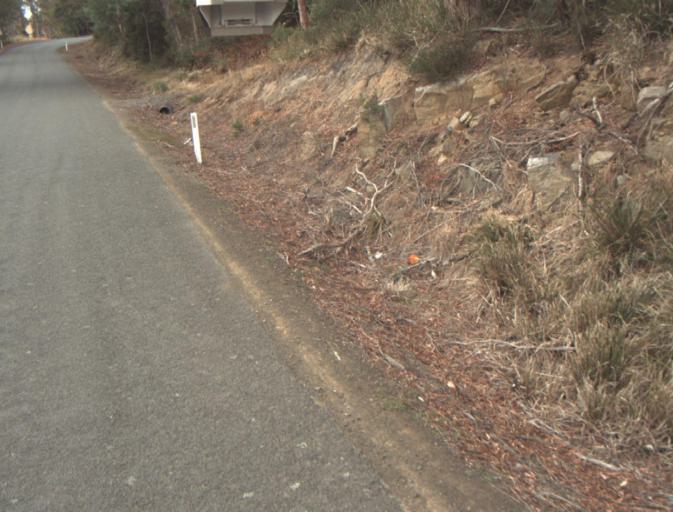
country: AU
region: Tasmania
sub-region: Launceston
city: Mayfield
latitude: -41.2389
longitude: 147.1967
